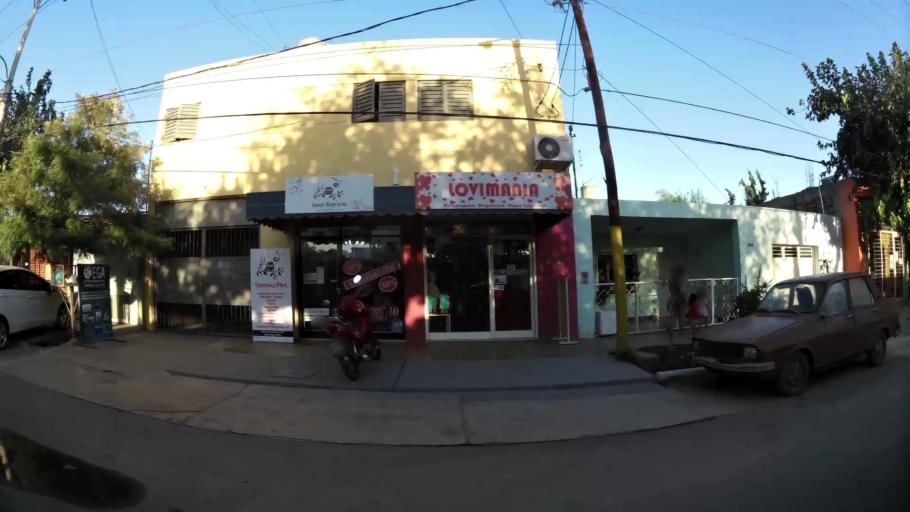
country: AR
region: San Juan
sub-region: Departamento de Santa Lucia
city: Santa Lucia
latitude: -31.5399
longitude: -68.4938
